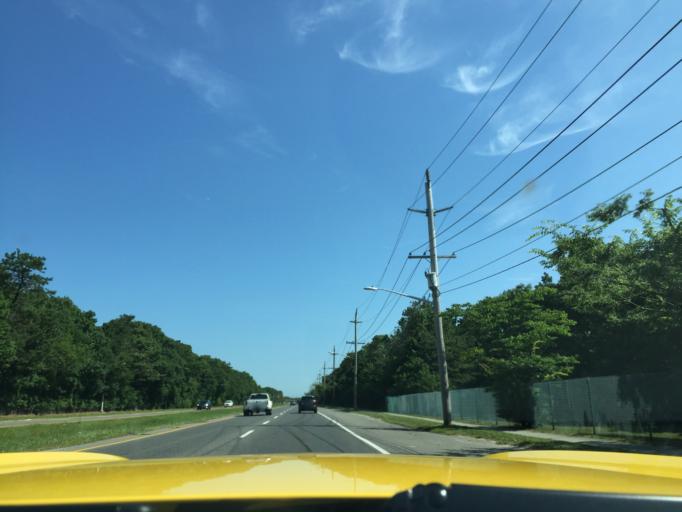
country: US
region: New York
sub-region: Suffolk County
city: Mastic Beach
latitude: 40.7680
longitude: -72.8690
